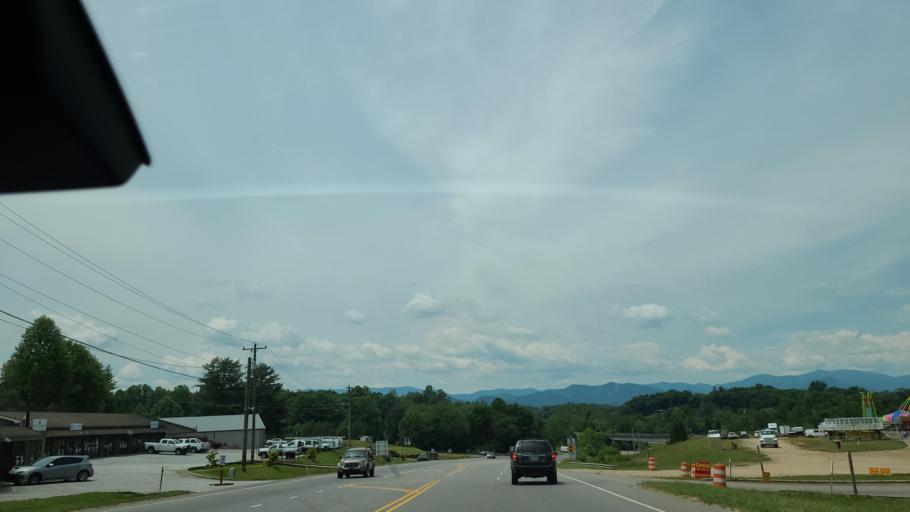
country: US
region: North Carolina
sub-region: Macon County
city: Franklin
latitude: 35.1765
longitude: -83.3539
